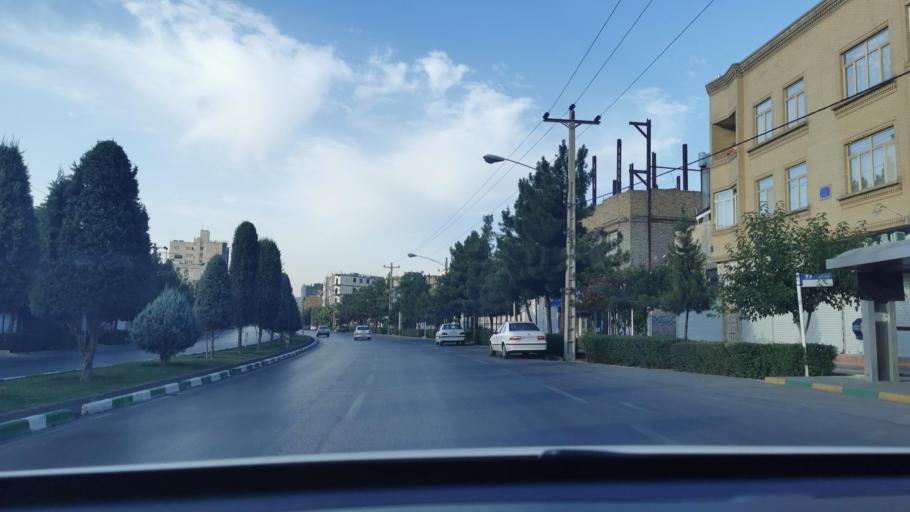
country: IR
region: Razavi Khorasan
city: Mashhad
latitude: 36.3565
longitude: 59.5019
